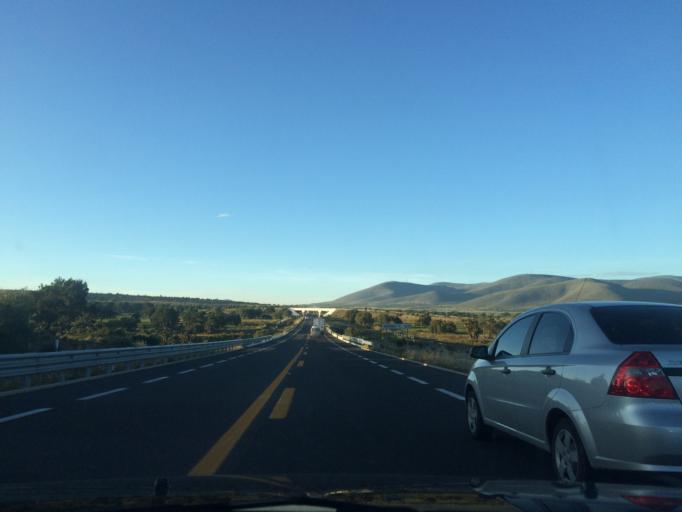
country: MX
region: Puebla
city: Cuacnopalan
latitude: 18.7774
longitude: -97.4867
